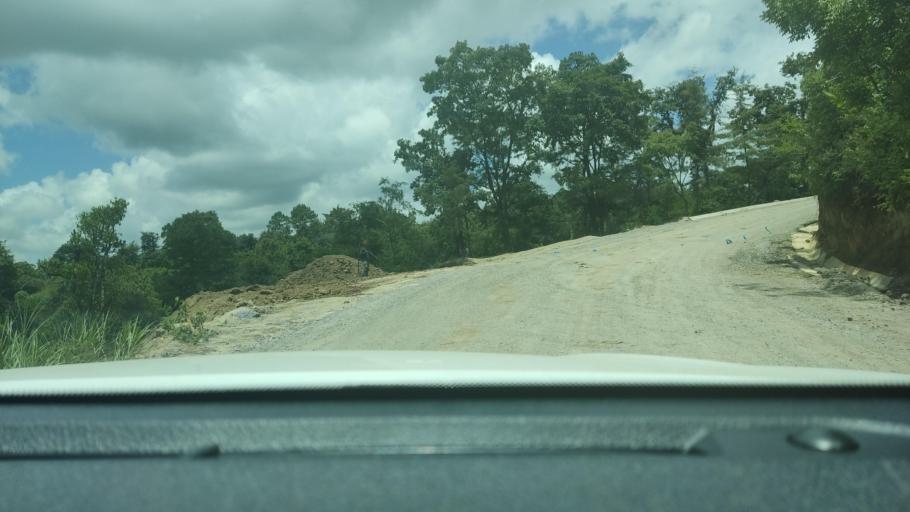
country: GT
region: Chimaltenango
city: San Martin Jilotepeque
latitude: 14.7969
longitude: -90.8137
